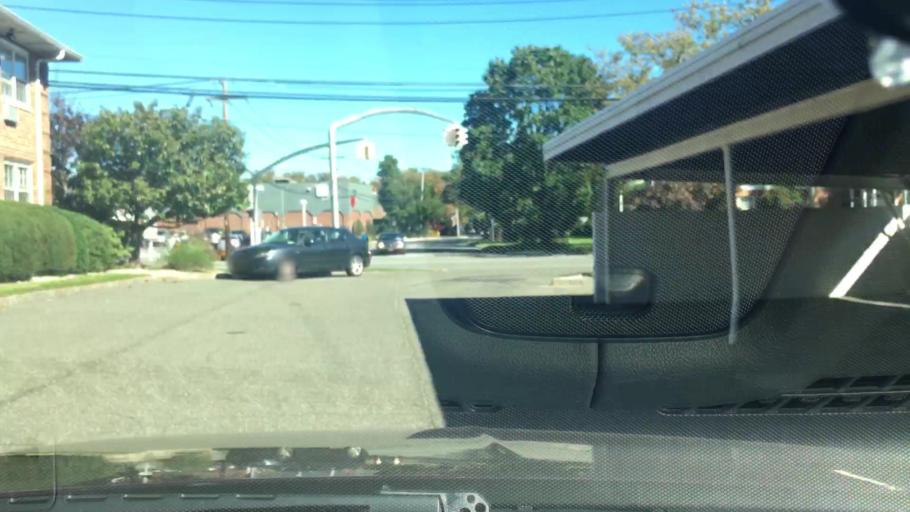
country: US
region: New York
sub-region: Nassau County
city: Port Washington North
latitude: 40.8402
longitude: -73.7054
